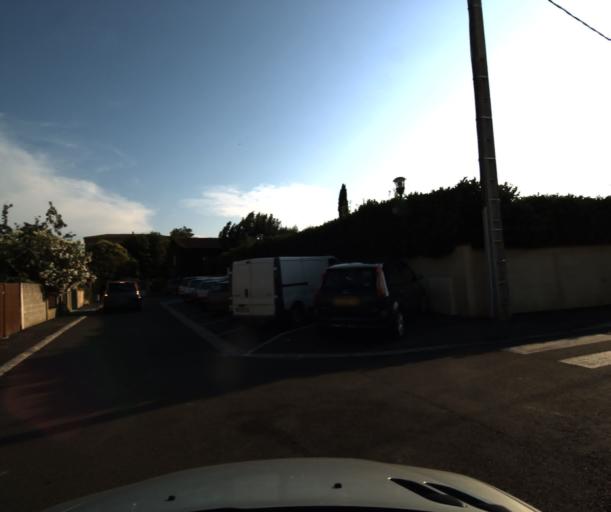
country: FR
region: Midi-Pyrenees
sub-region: Departement de la Haute-Garonne
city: Roquettes
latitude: 43.4805
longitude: 1.3831
